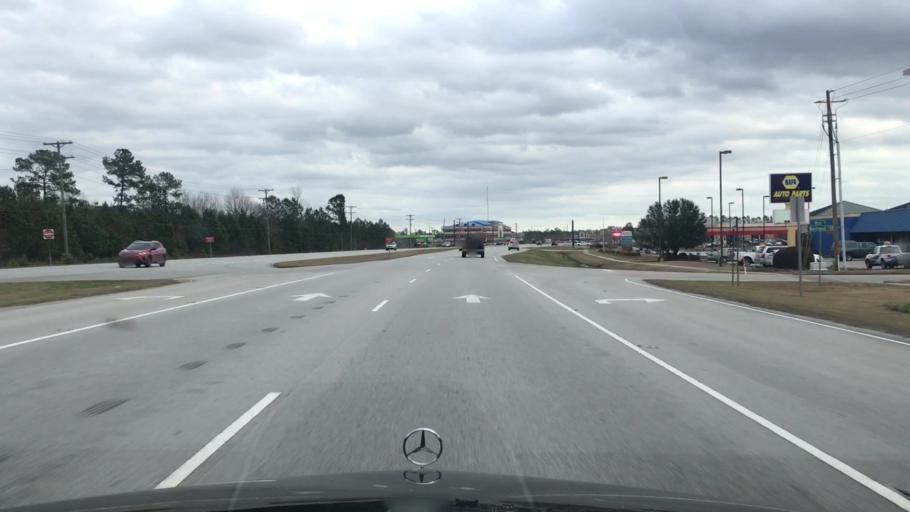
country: US
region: North Carolina
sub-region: Onslow County
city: Half Moon
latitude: 34.8010
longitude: -77.4213
